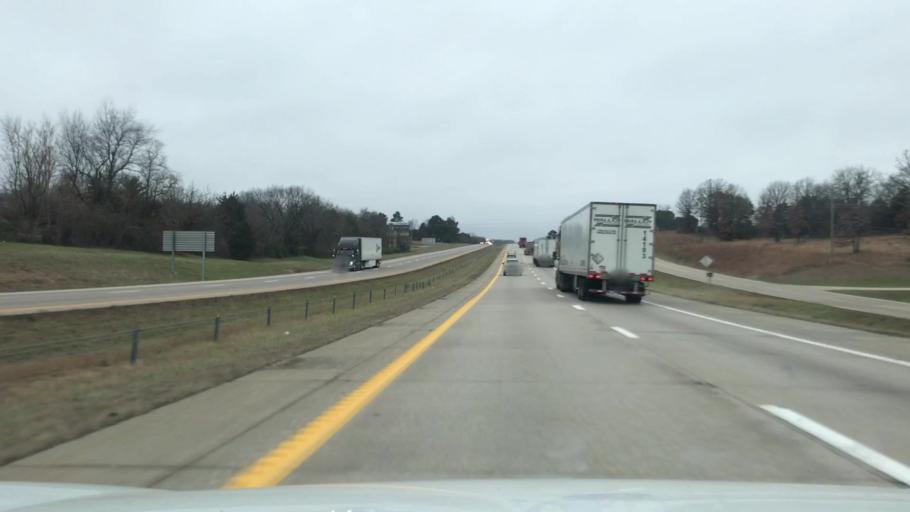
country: US
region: Missouri
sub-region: Crawford County
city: Bourbon
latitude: 38.1512
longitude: -91.2561
